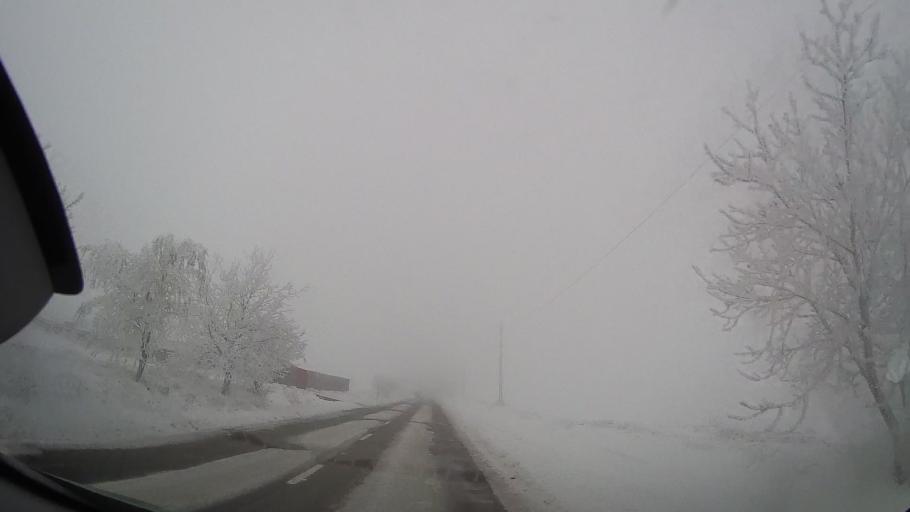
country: RO
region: Neamt
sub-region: Comuna Valea Ursului
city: Valea Ursului
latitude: 46.8035
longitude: 27.0728
